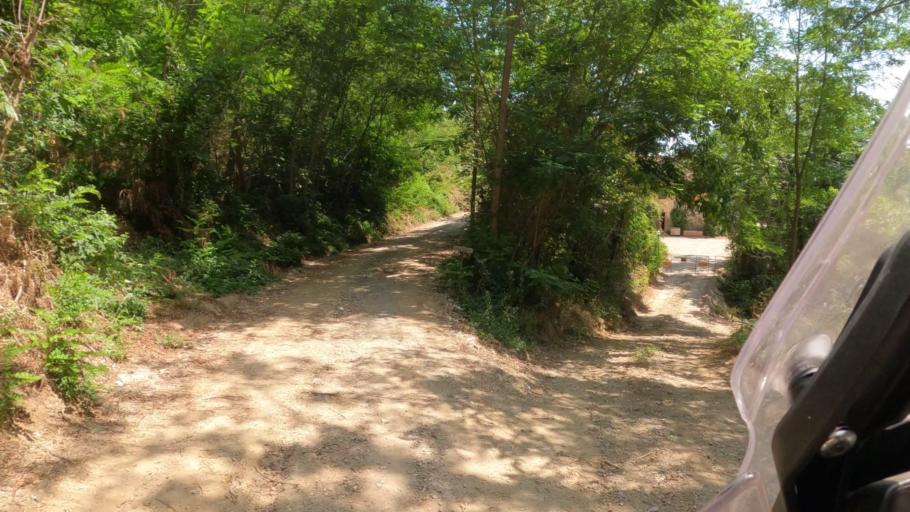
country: IT
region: Piedmont
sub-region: Provincia di Alessandria
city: Cassinelle-Concentrico
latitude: 44.5680
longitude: 8.5645
